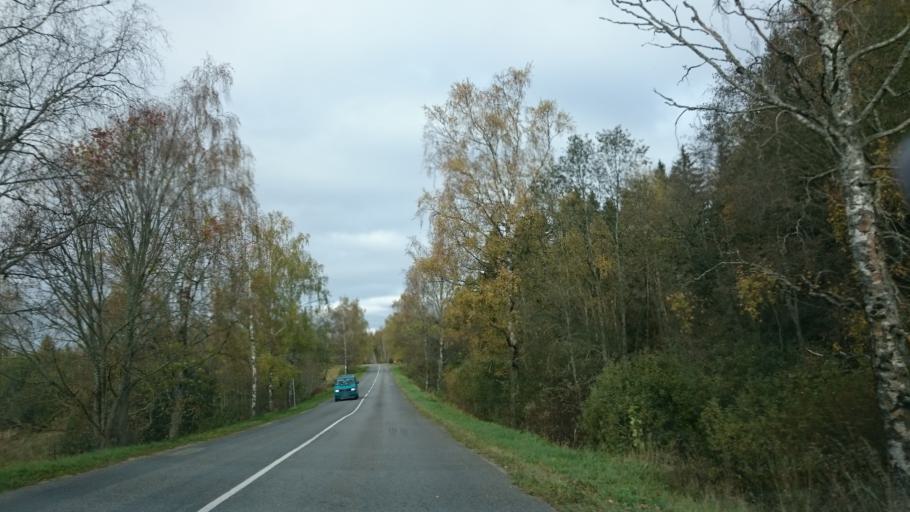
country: LV
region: Amatas Novads
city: Drabesi
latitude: 57.2740
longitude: 25.2713
